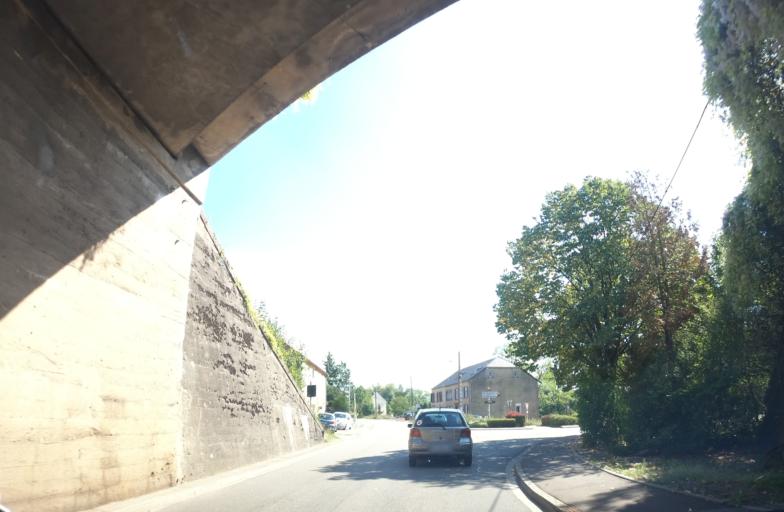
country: FR
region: Lorraine
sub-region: Departement de la Moselle
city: Diebling
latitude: 49.1050
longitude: 6.9591
